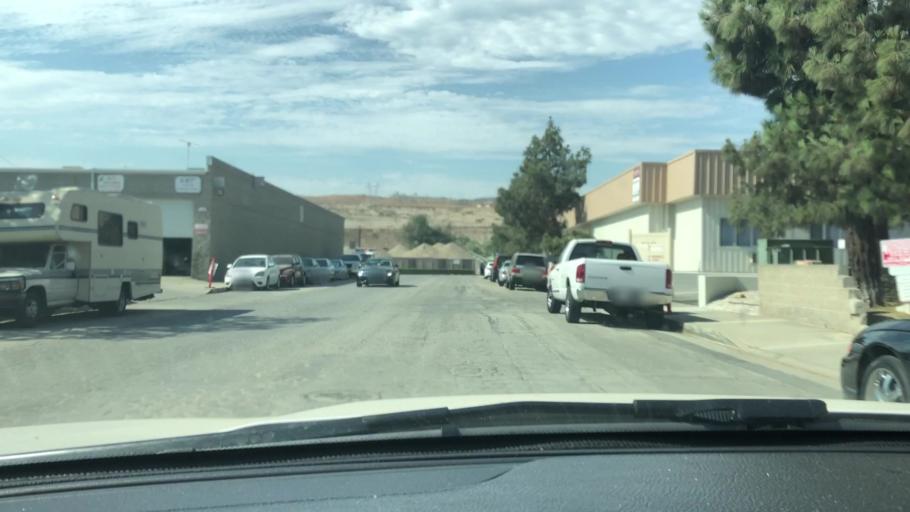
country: US
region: California
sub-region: Los Angeles County
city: Santa Clarita
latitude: 34.4242
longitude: -118.5005
